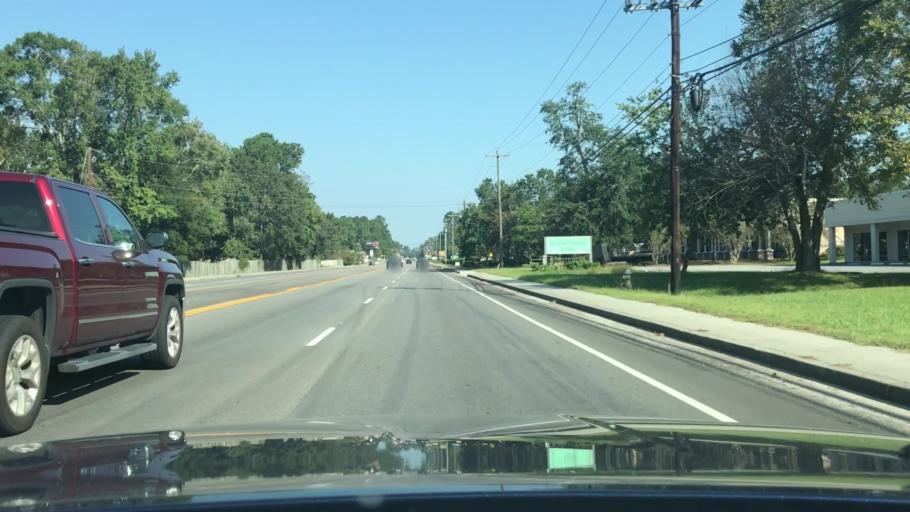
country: US
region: South Carolina
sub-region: Dorchester County
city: Centerville
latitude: 32.9788
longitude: -80.1734
